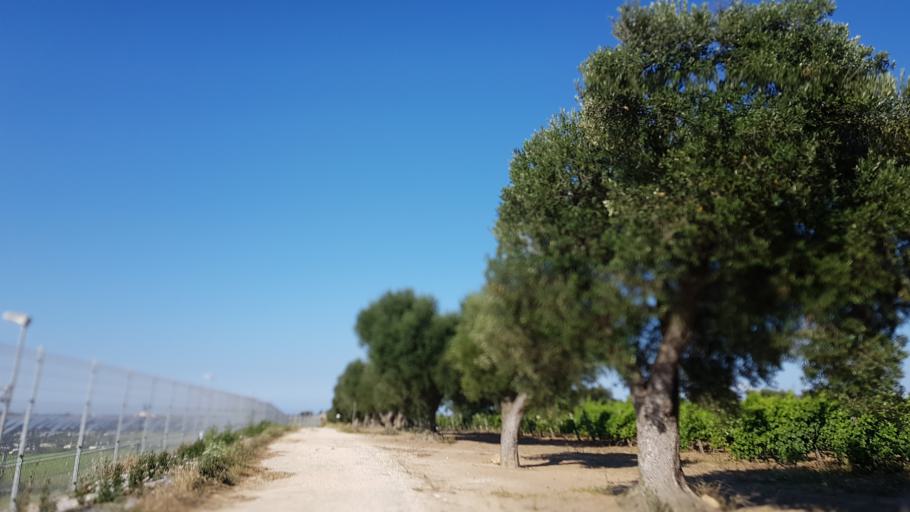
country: IT
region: Apulia
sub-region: Provincia di Brindisi
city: La Rosa
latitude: 40.5912
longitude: 17.9907
